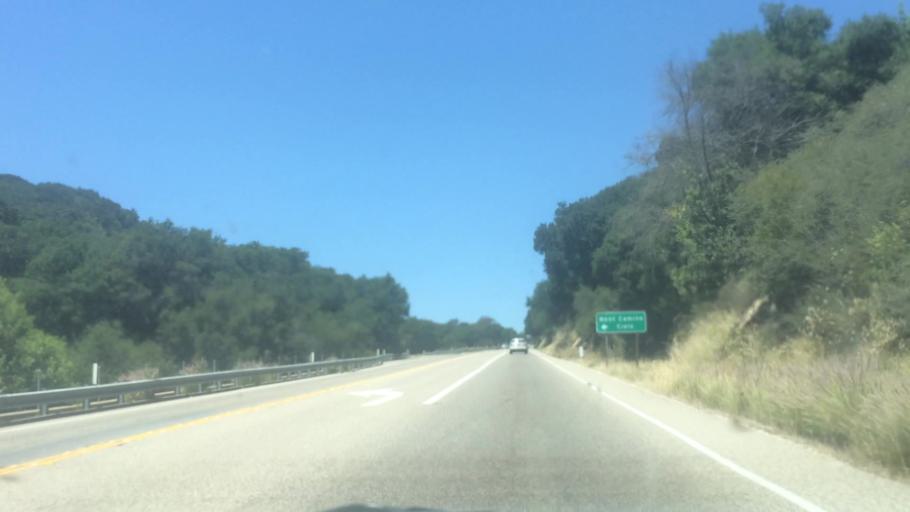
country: US
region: California
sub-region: Santa Barbara County
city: Goleta
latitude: 34.5042
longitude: -119.8109
